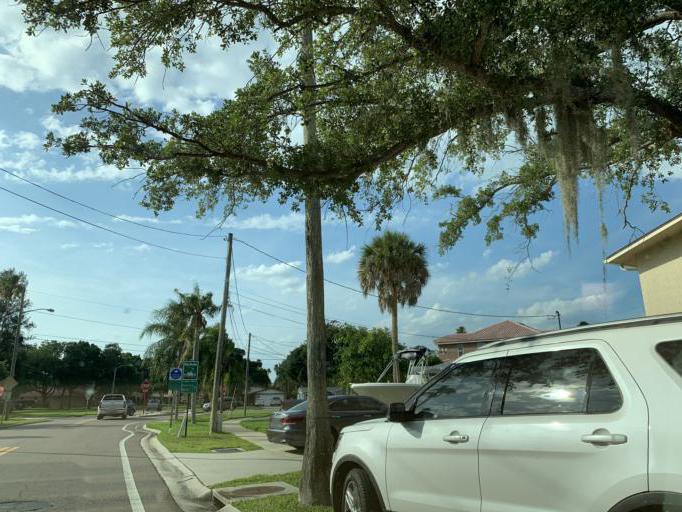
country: US
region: Florida
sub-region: Pinellas County
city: Gandy
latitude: 27.8222
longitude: -82.6080
